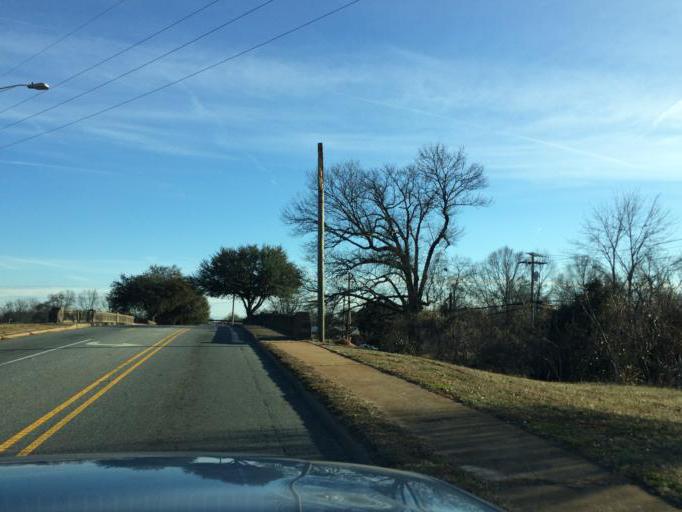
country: US
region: North Carolina
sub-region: Rutherford County
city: Forest City
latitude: 35.3296
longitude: -81.8630
